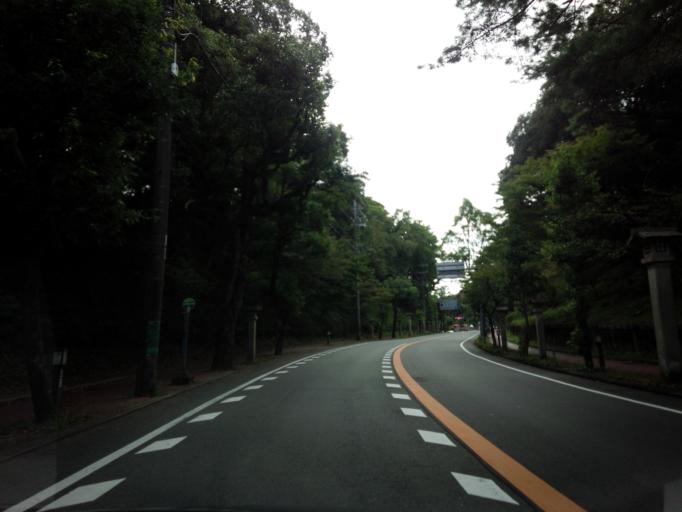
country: JP
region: Mie
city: Ise
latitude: 34.4859
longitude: 136.7255
